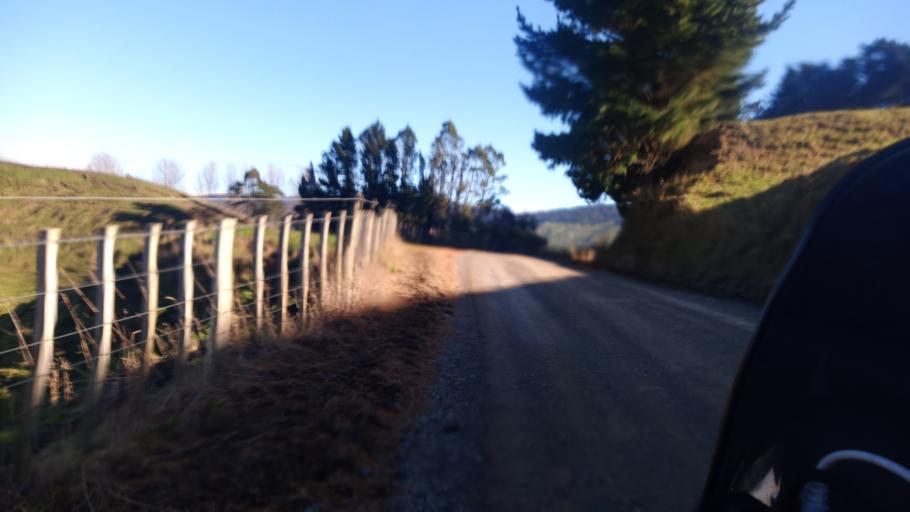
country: NZ
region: Hawke's Bay
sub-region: Wairoa District
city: Wairoa
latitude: -38.7870
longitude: 177.2725
